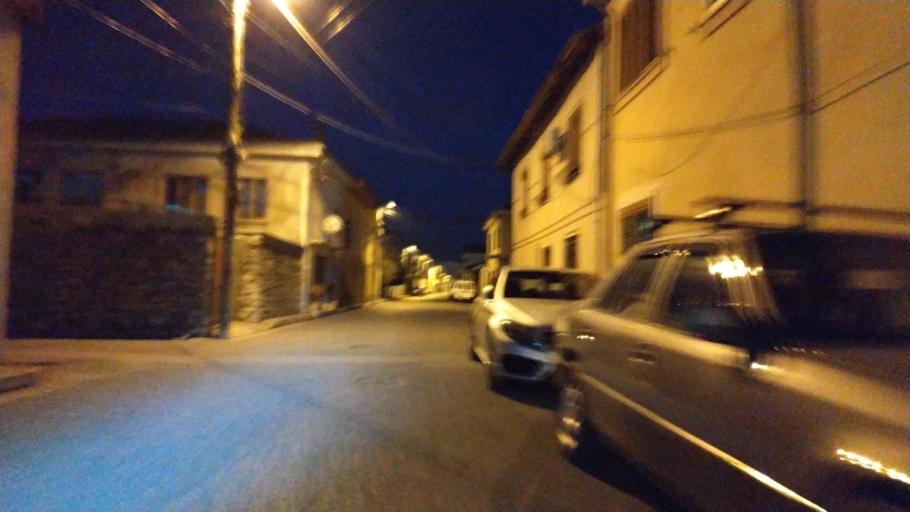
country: AL
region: Shkoder
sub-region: Rrethi i Shkodres
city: Shkoder
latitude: 42.0639
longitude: 19.5049
